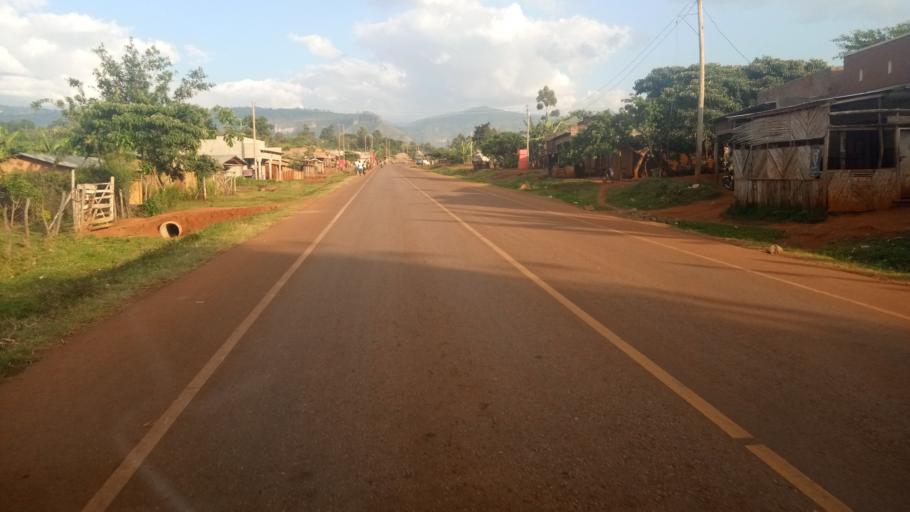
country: UG
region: Eastern Region
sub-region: Sironko District
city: Sironko
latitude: 1.3223
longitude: 34.3344
